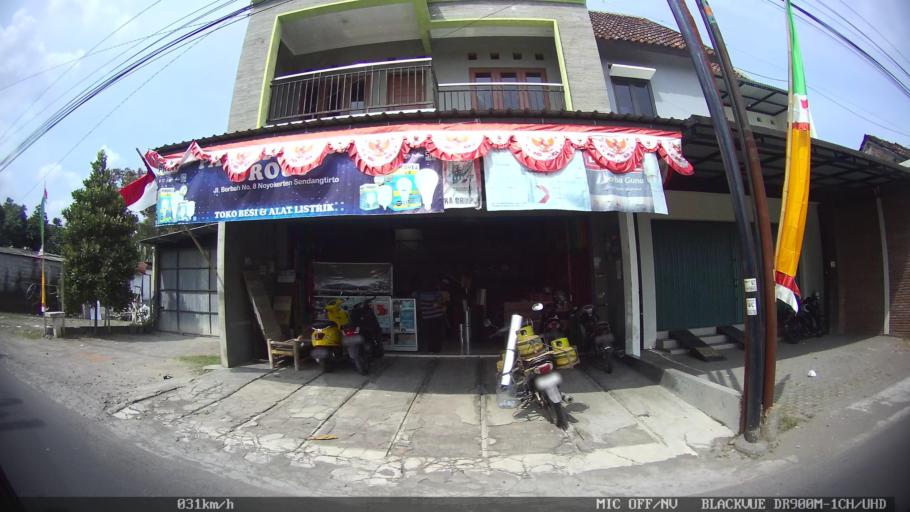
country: ID
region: Daerah Istimewa Yogyakarta
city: Depok
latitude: -7.8048
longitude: 110.4284
